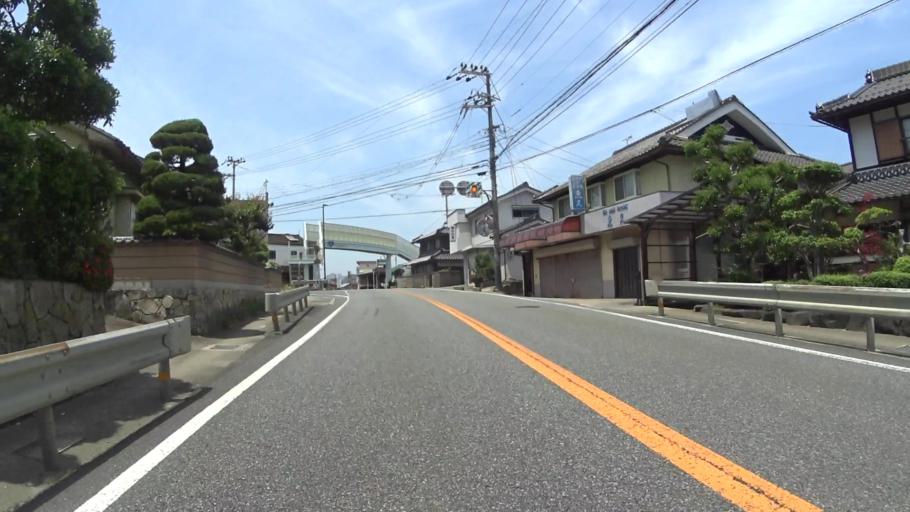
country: JP
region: Kyoto
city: Ayabe
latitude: 35.2157
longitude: 135.2367
